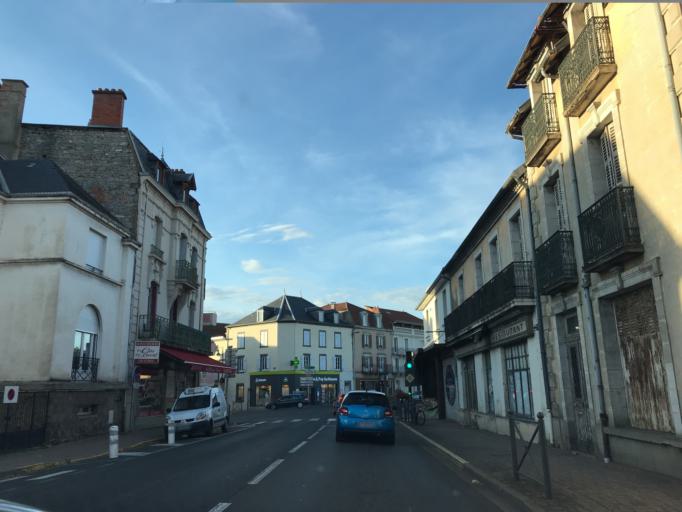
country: FR
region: Auvergne
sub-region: Departement du Puy-de-Dome
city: Puy-Guillaume
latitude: 45.9593
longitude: 3.4744
